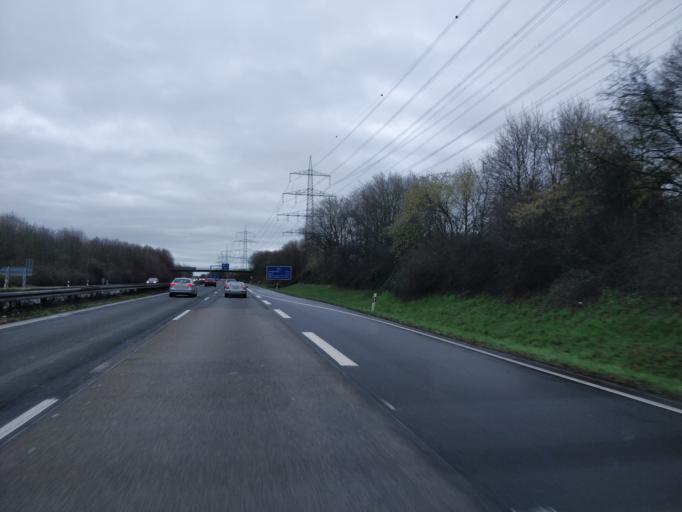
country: DE
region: North Rhine-Westphalia
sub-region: Regierungsbezirk Koln
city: Troisdorf
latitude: 50.8178
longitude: 7.1118
